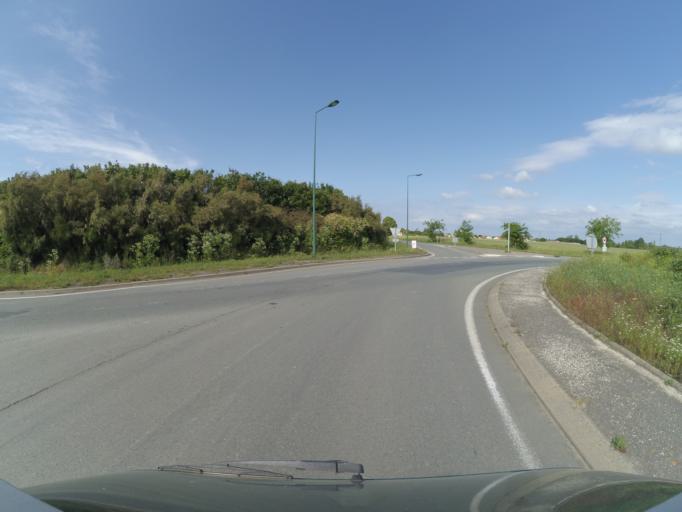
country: FR
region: Poitou-Charentes
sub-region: Departement de la Charente-Maritime
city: Saint-Xandre
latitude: 46.2345
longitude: -1.0737
